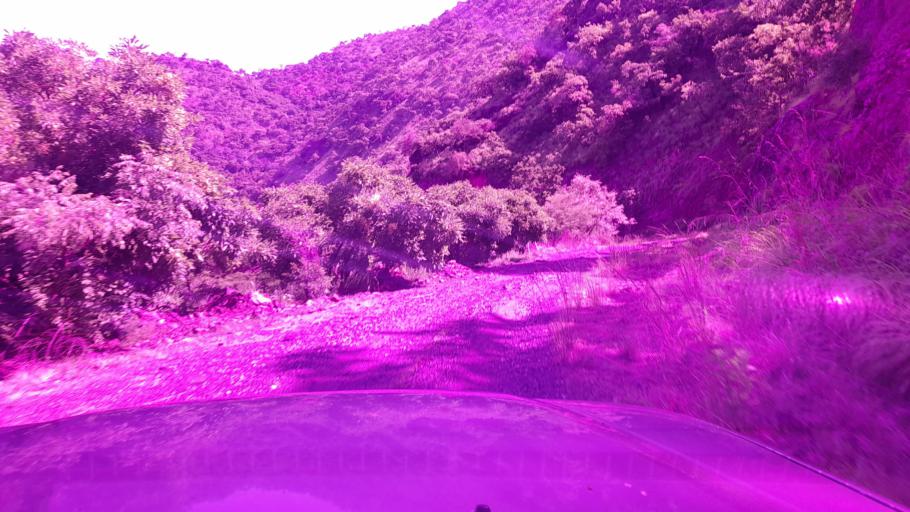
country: ET
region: Southern Nations, Nationalities, and People's Region
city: K'olito
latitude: 7.7765
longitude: 37.5558
